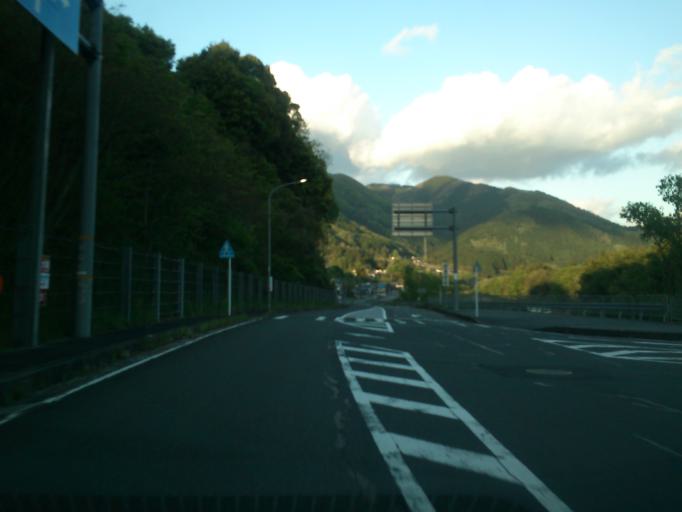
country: JP
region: Kyoto
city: Ayabe
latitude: 35.2699
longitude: 135.3842
